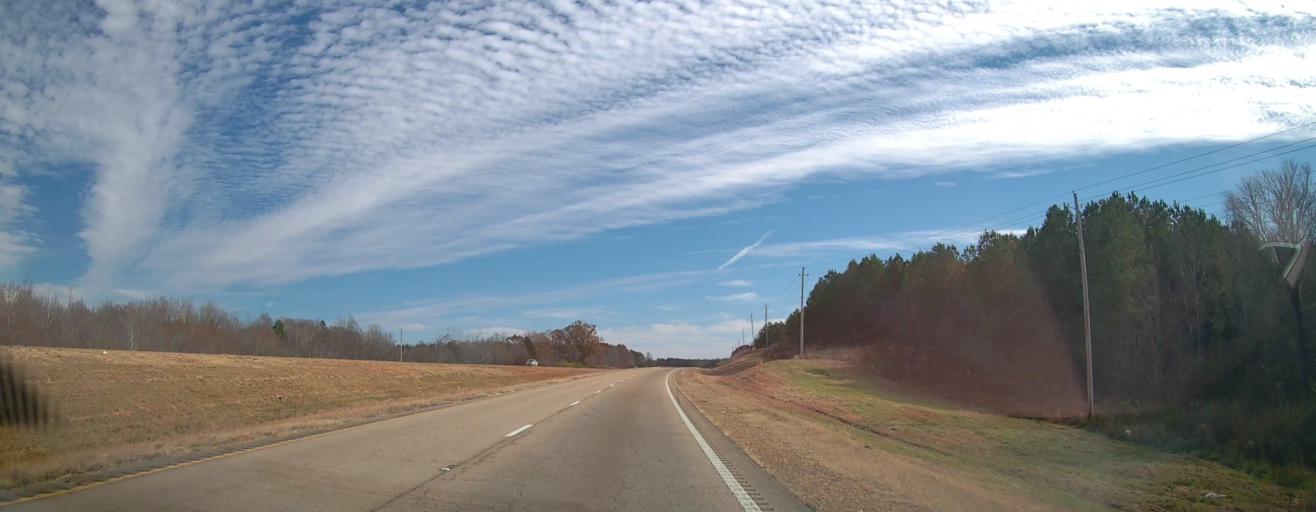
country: US
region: Mississippi
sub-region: Alcorn County
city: Corinth
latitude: 34.9359
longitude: -88.7294
